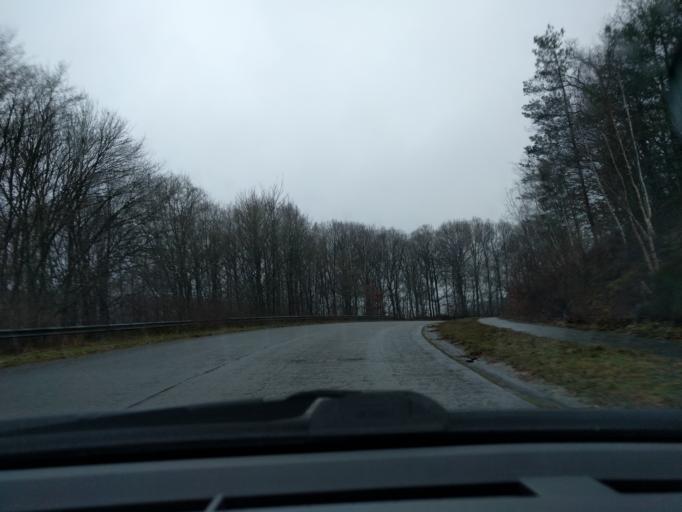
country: BE
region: Wallonia
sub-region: Province de Namur
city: Couvin
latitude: 50.0249
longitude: 4.5364
